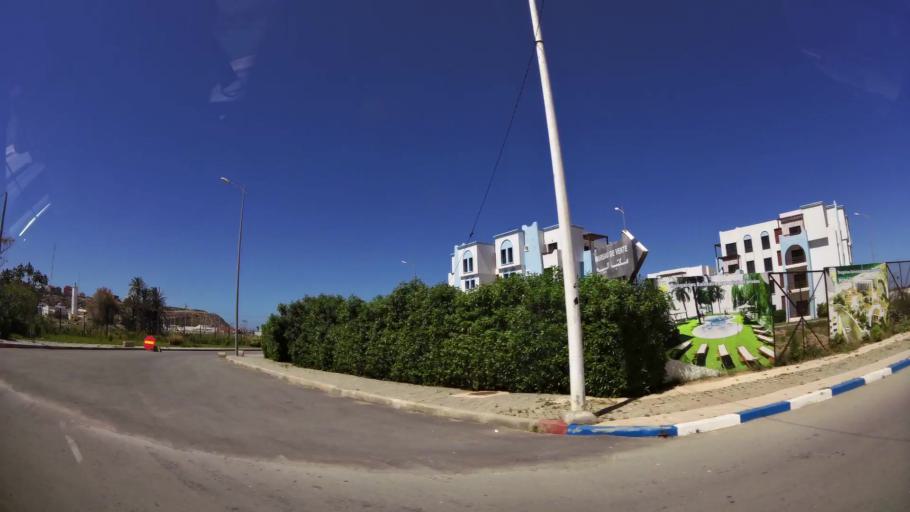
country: MA
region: Oriental
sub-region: Berkane-Taourirt
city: Madagh
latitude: 35.1388
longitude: -2.4216
